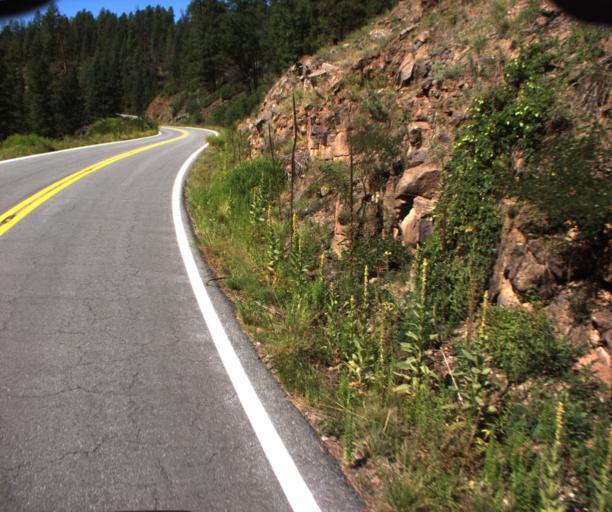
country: US
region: Arizona
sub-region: Apache County
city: Eagar
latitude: 33.7758
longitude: -109.1860
